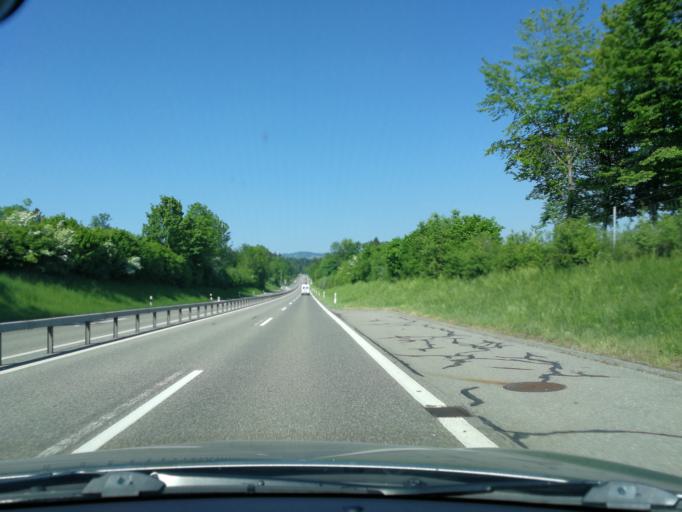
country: CH
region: Zurich
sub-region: Bezirk Hinwil
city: Binzikon
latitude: 47.2890
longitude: 8.7633
